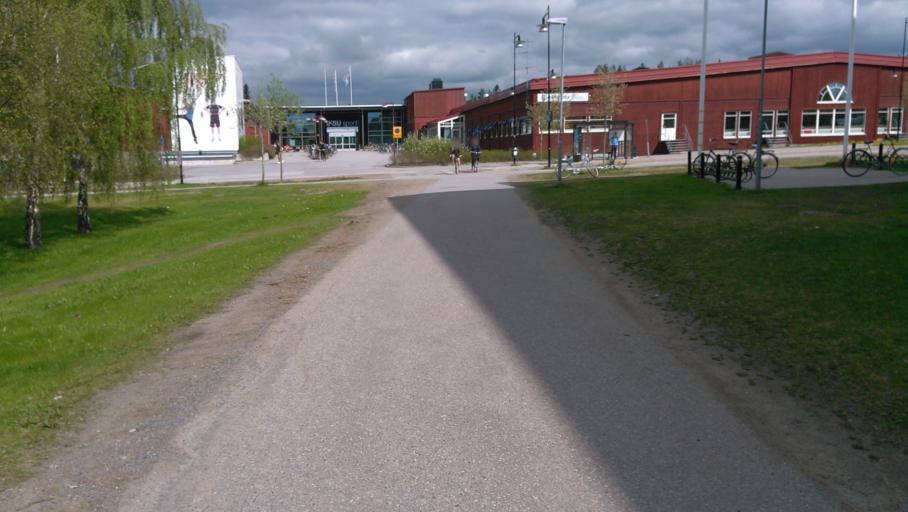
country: SE
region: Vaesterbotten
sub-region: Umea Kommun
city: Umea
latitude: 63.8174
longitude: 20.3183
